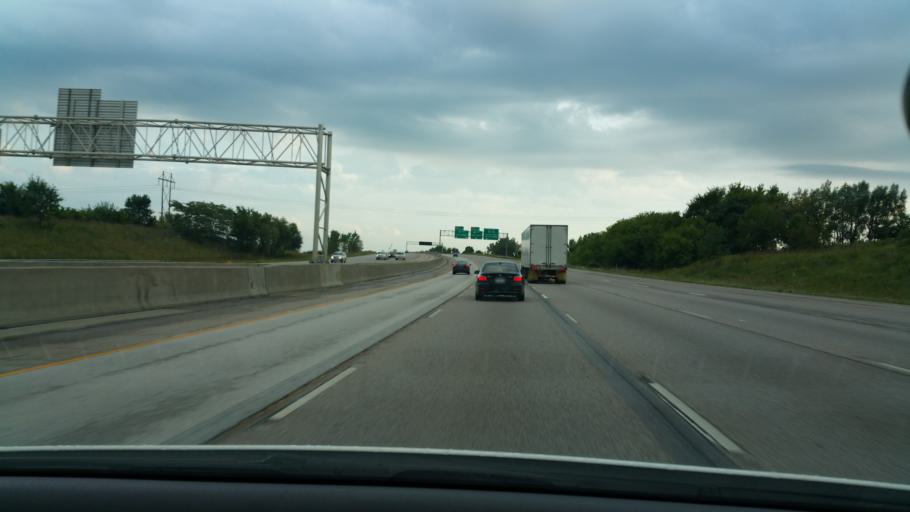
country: US
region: Iowa
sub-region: Polk County
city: Saylorville
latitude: 41.6749
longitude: -93.5779
